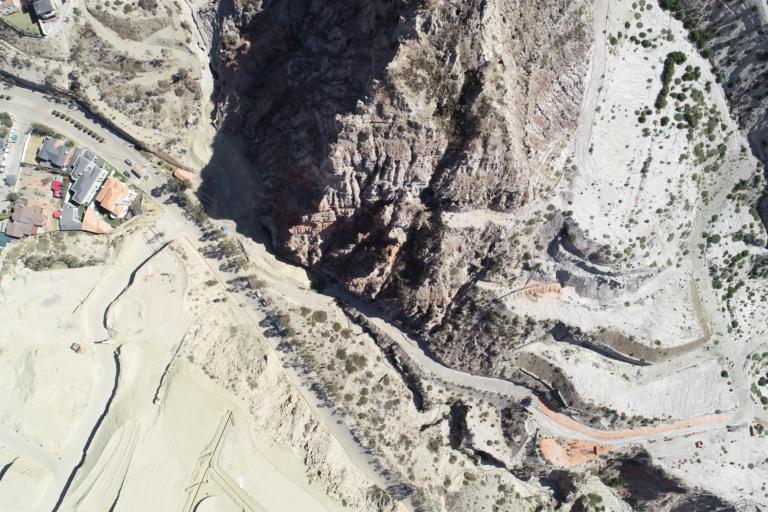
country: BO
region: La Paz
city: La Paz
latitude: -16.5563
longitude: -68.1090
